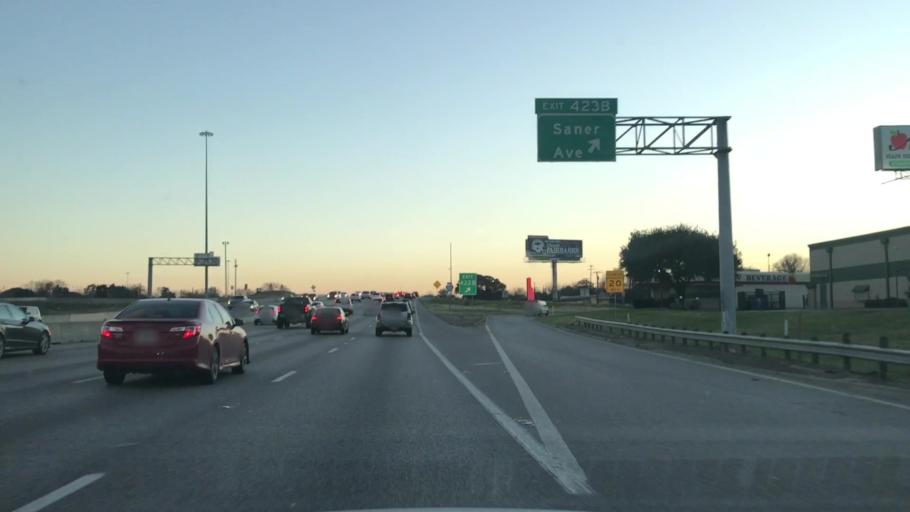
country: US
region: Texas
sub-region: Dallas County
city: Cockrell Hill
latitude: 32.7159
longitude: -96.8291
